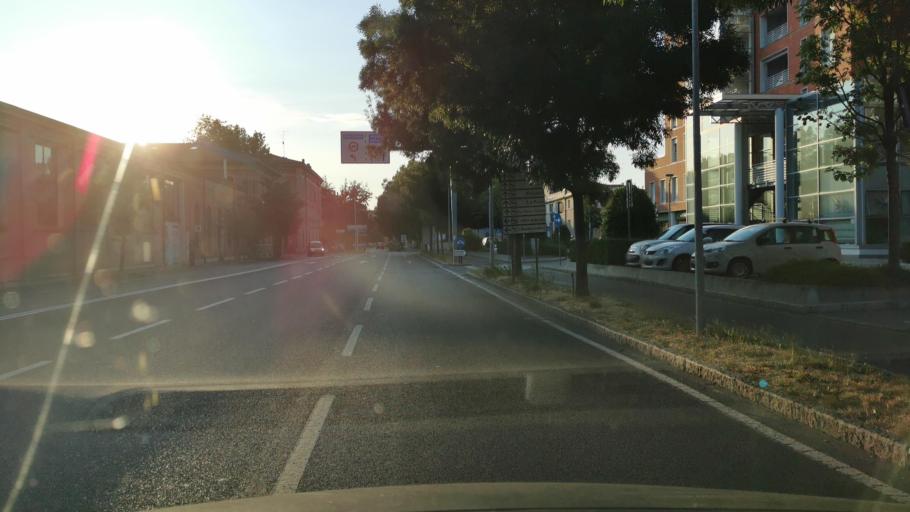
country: IT
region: Emilia-Romagna
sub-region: Provincia di Modena
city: Modena
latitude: 44.6497
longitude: 10.9384
